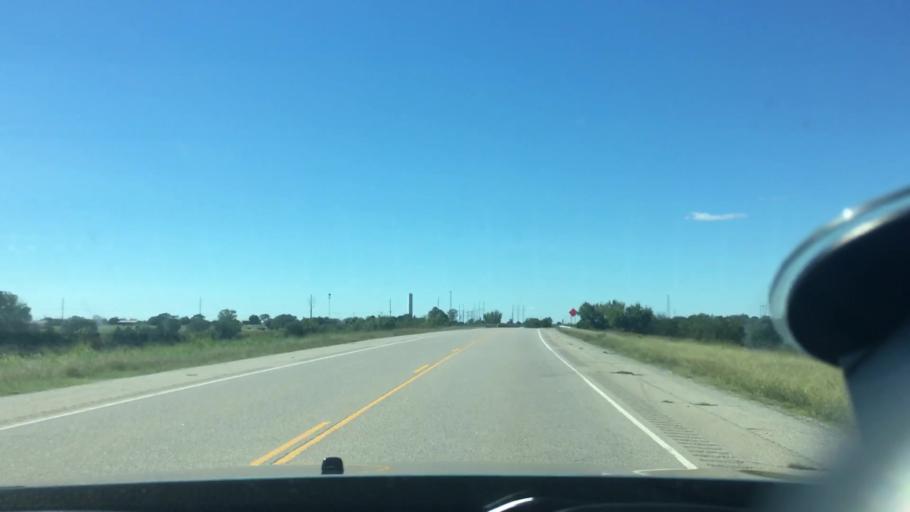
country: US
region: Oklahoma
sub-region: Coal County
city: Coalgate
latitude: 34.6114
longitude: -96.4313
